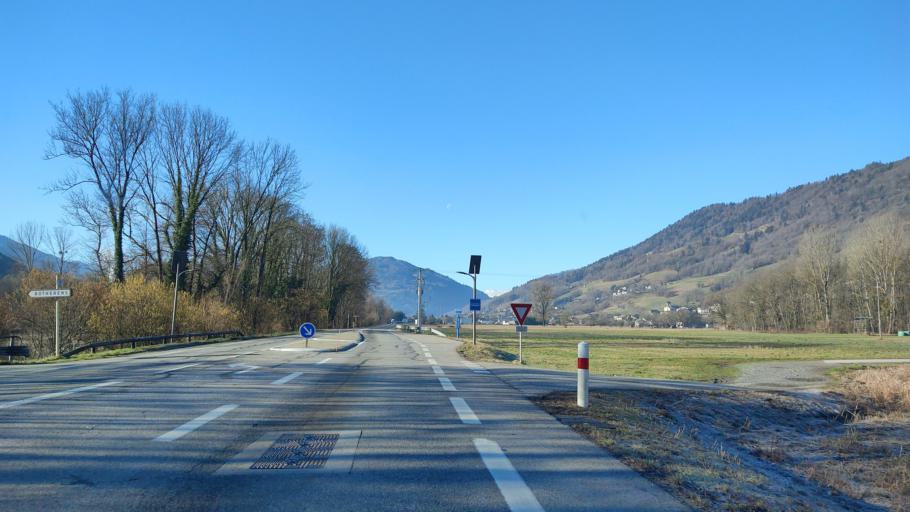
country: FR
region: Rhone-Alpes
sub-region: Departement de la Savoie
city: La Rochette
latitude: 45.4737
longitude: 6.1298
